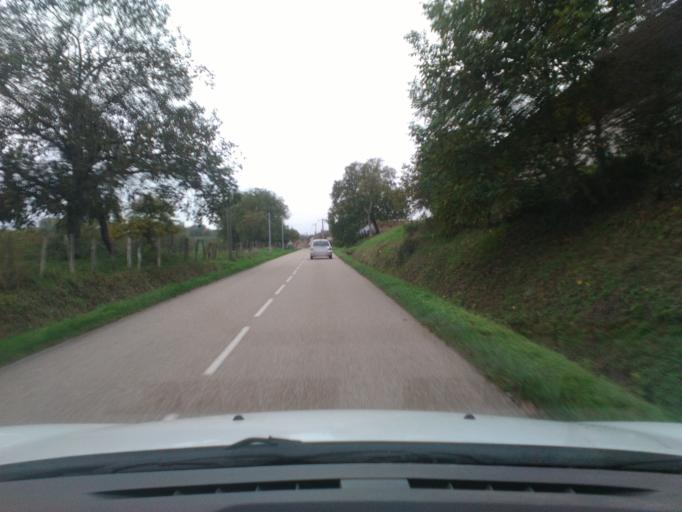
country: FR
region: Lorraine
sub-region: Departement des Vosges
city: Vincey
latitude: 48.3032
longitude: 6.2746
